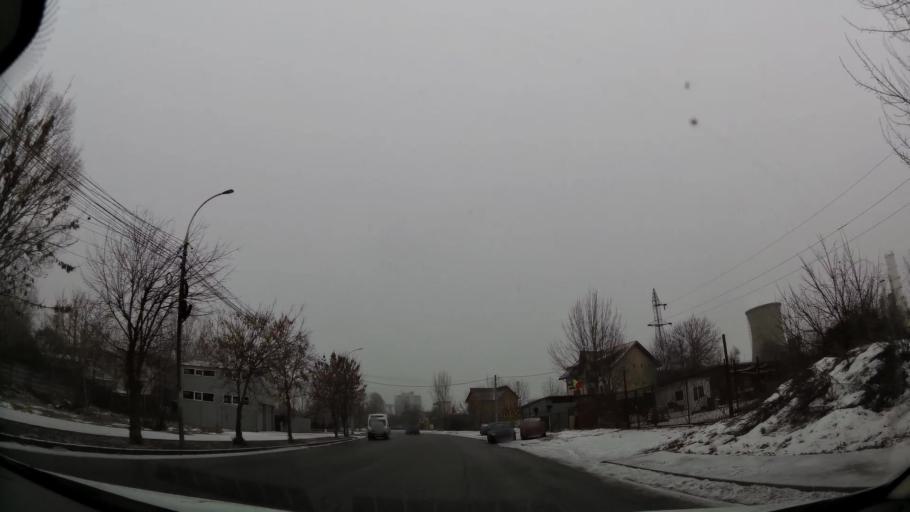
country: RO
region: Dambovita
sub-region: Municipiul Targoviste
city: Targoviste
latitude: 44.9128
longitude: 25.4444
